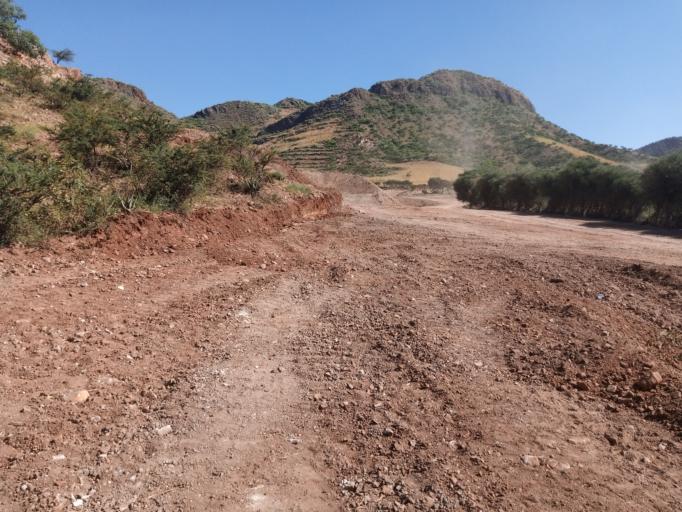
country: ET
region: Tigray
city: Korem
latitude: 12.6687
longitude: 39.0209
